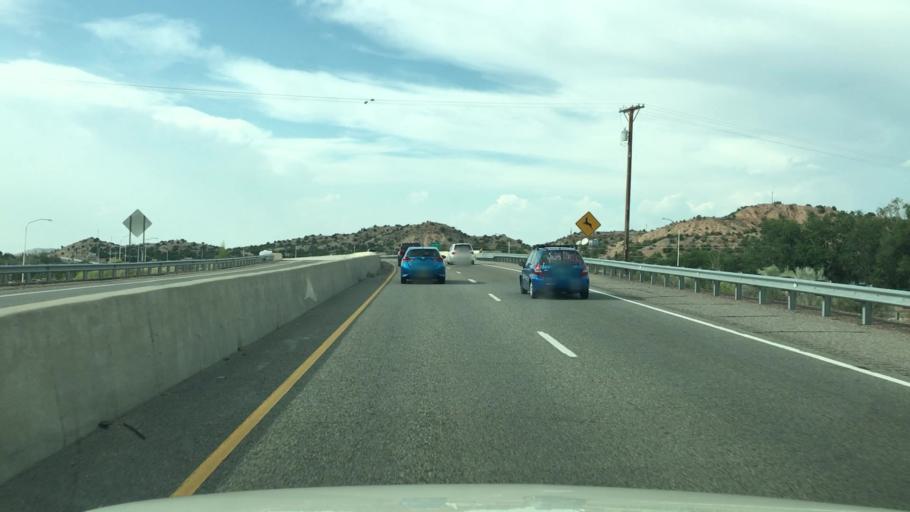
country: US
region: New Mexico
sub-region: Santa Fe County
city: Santa Fe
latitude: 35.7822
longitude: -105.9479
